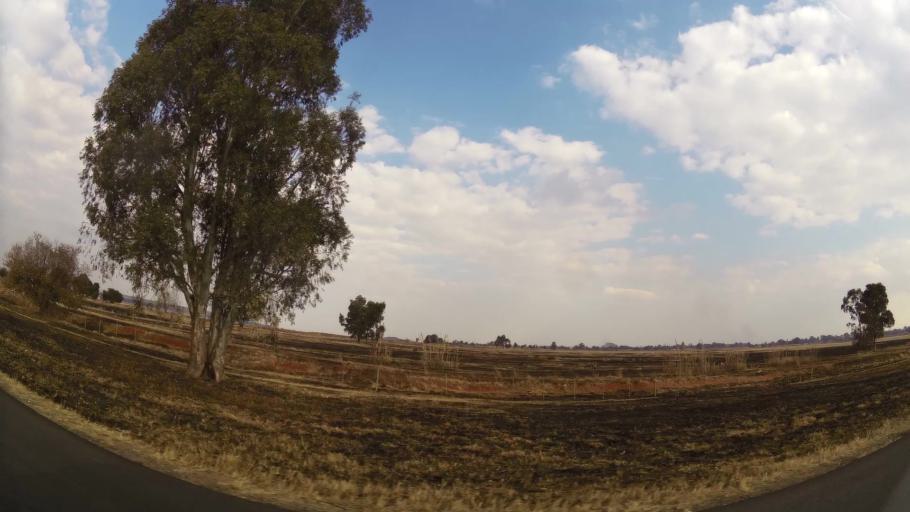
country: ZA
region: Gauteng
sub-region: Ekurhuleni Metropolitan Municipality
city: Springs
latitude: -26.2696
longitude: 28.4876
